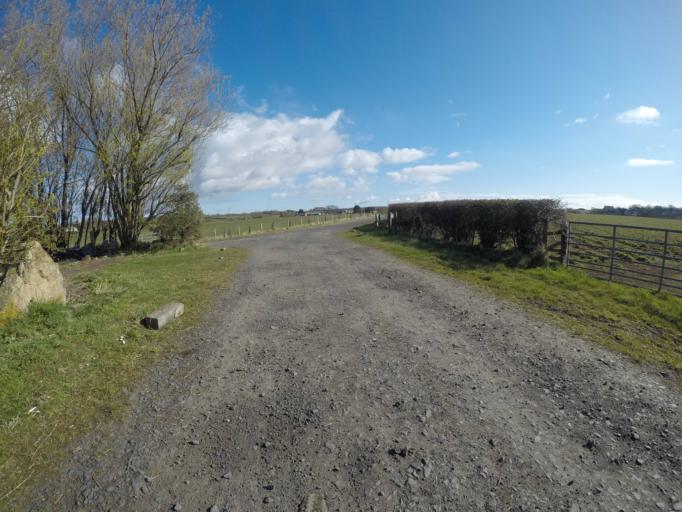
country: GB
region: Scotland
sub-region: North Ayrshire
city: Irvine
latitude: 55.6519
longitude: -4.6570
